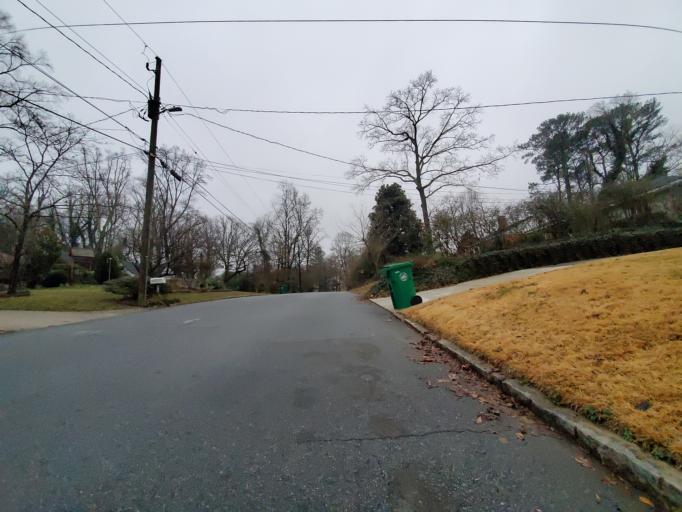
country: US
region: Georgia
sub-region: DeKalb County
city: North Decatur
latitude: 33.7945
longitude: -84.3043
